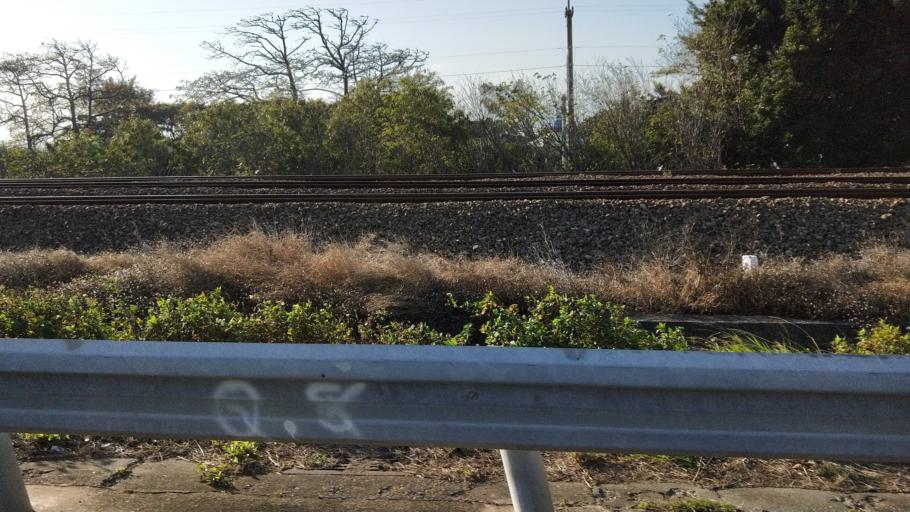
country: TW
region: Taiwan
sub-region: Miaoli
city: Miaoli
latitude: 24.5358
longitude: 120.6945
